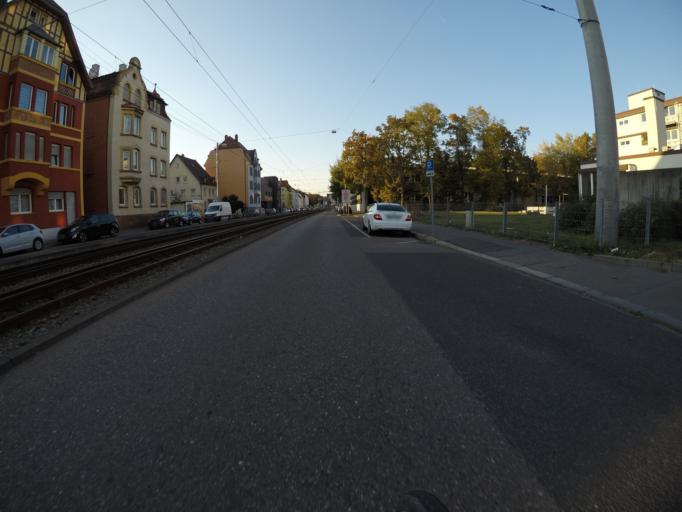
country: DE
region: Baden-Wuerttemberg
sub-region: Regierungsbezirk Stuttgart
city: Stuttgart-Ost
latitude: 48.7696
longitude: 9.2471
